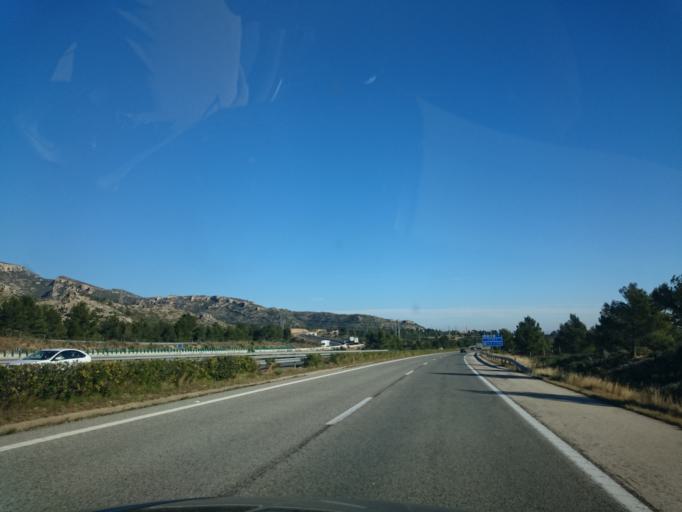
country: ES
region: Catalonia
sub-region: Provincia de Tarragona
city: l'Ametlla de Mar
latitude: 40.9797
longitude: 0.8850
